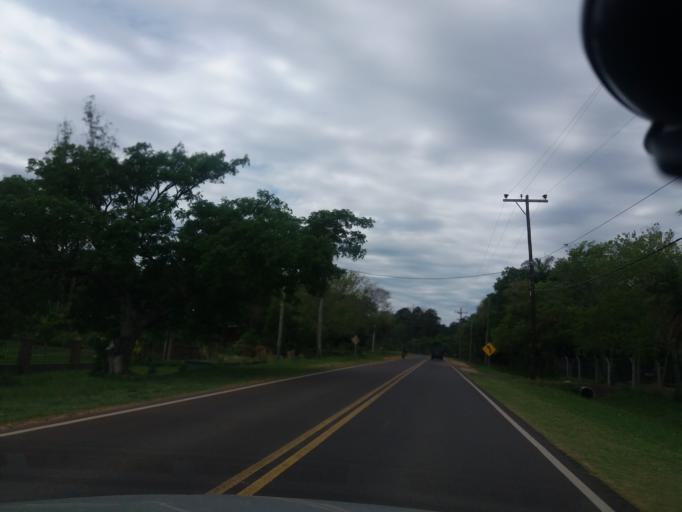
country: AR
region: Corrientes
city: Riachuelo
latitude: -27.4580
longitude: -58.7065
